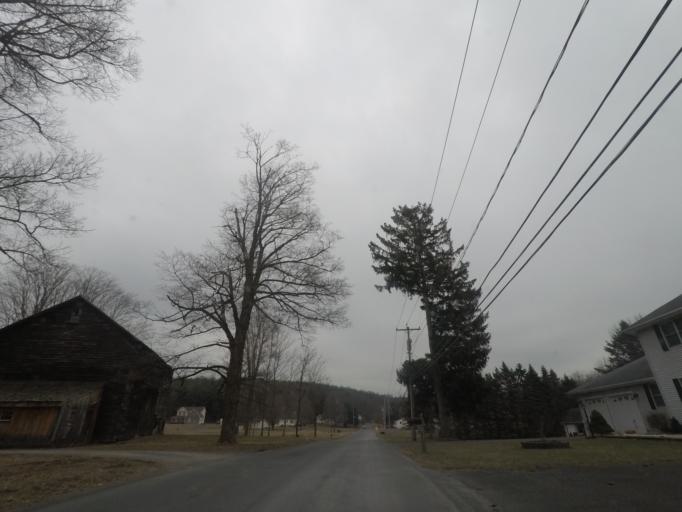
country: US
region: New York
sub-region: Rensselaer County
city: East Greenbush
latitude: 42.5797
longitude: -73.6739
